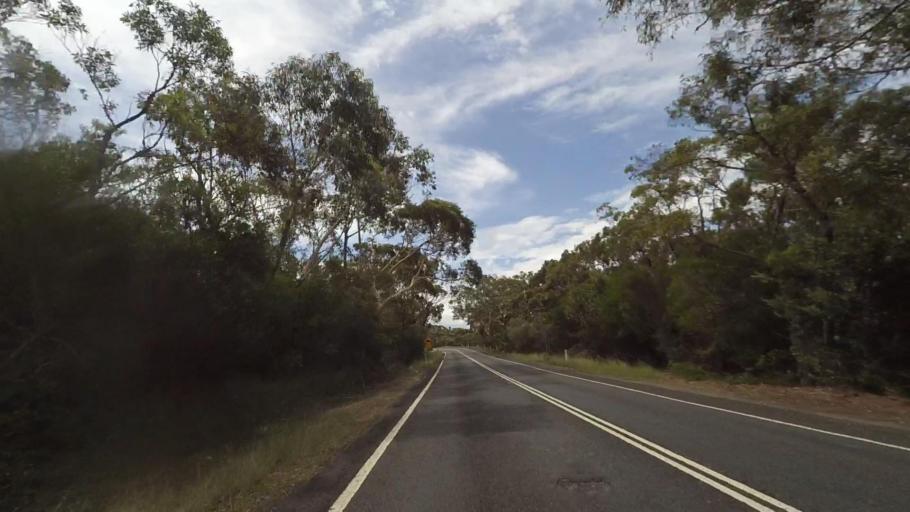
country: AU
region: New South Wales
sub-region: Sutherland Shire
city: Grays Point
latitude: -34.0838
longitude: 151.0636
